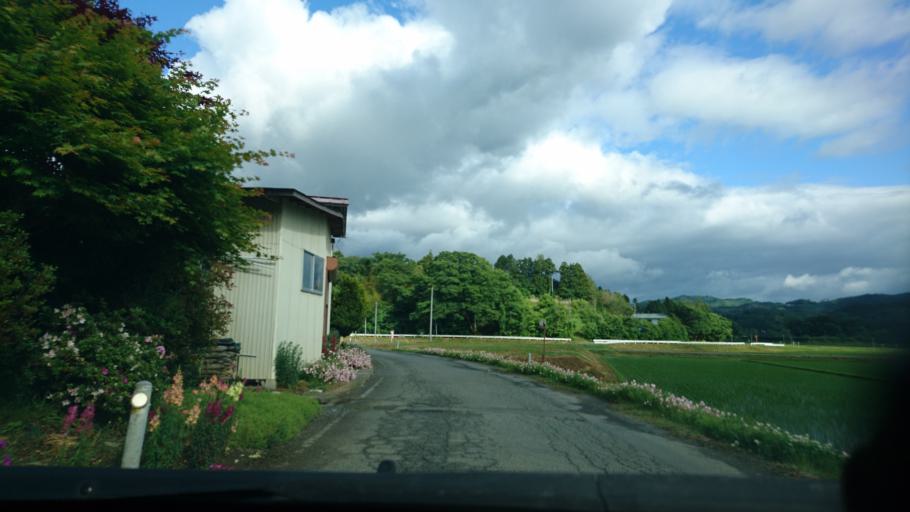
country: JP
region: Iwate
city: Ichinoseki
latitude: 38.8581
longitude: 141.2853
